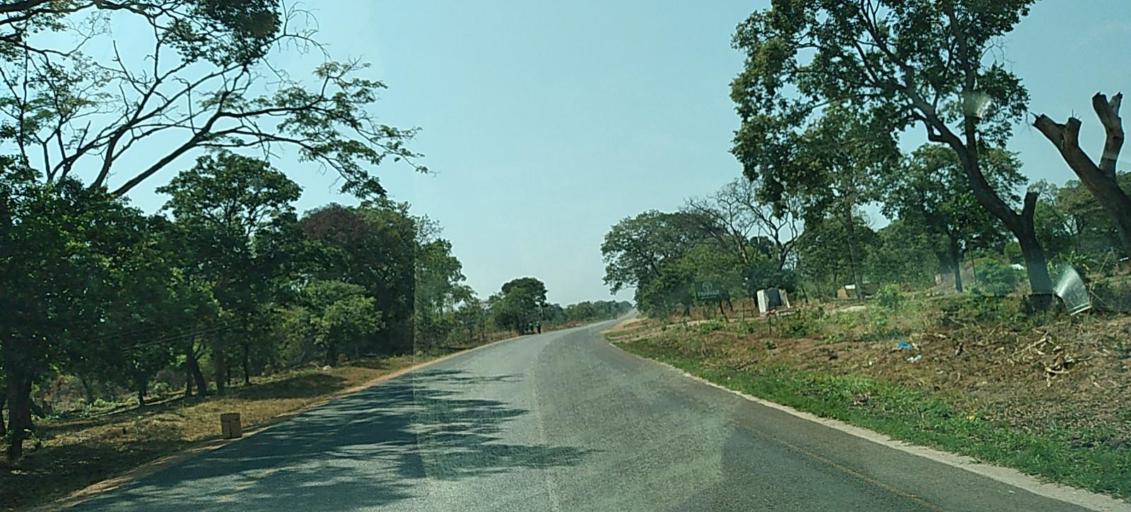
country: ZM
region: North-Western
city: Solwezi
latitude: -12.2991
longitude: 25.8297
